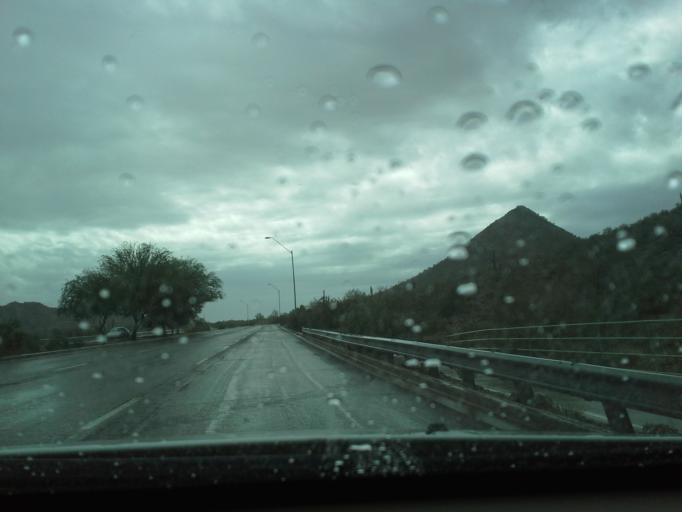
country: US
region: Arizona
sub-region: Maricopa County
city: Fountain Hills
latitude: 33.5809
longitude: -111.7803
